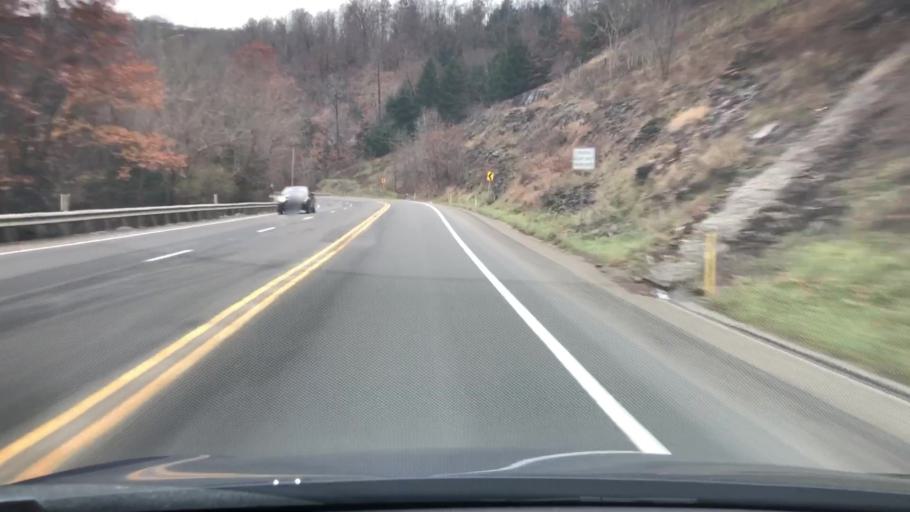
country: US
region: Pennsylvania
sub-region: Armstrong County
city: Kittanning
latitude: 40.9638
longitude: -79.3626
